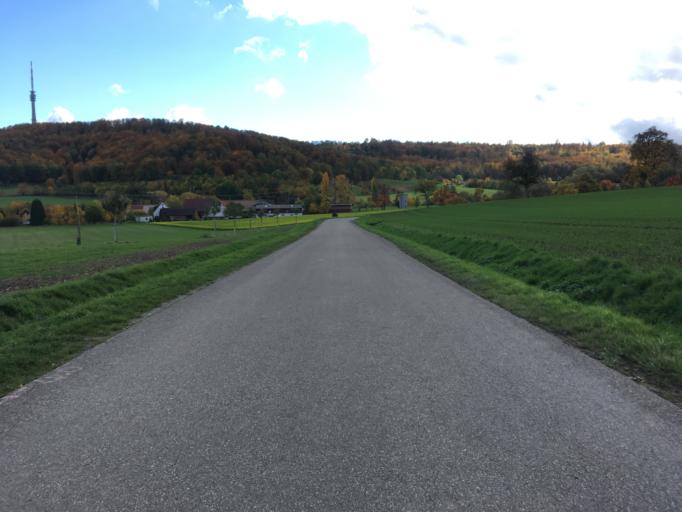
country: DE
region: Baden-Wuerttemberg
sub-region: Regierungsbezirk Stuttgart
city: Waldenburg
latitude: 49.1930
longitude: 9.6523
